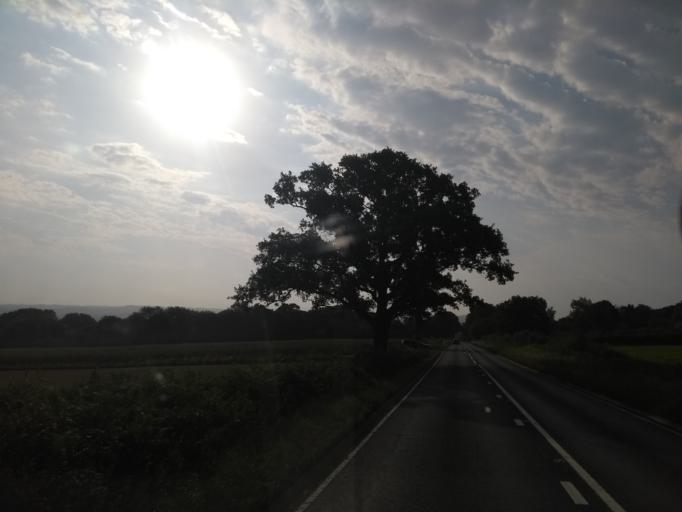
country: GB
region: England
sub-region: Devon
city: Axminster
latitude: 50.7834
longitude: -3.0450
